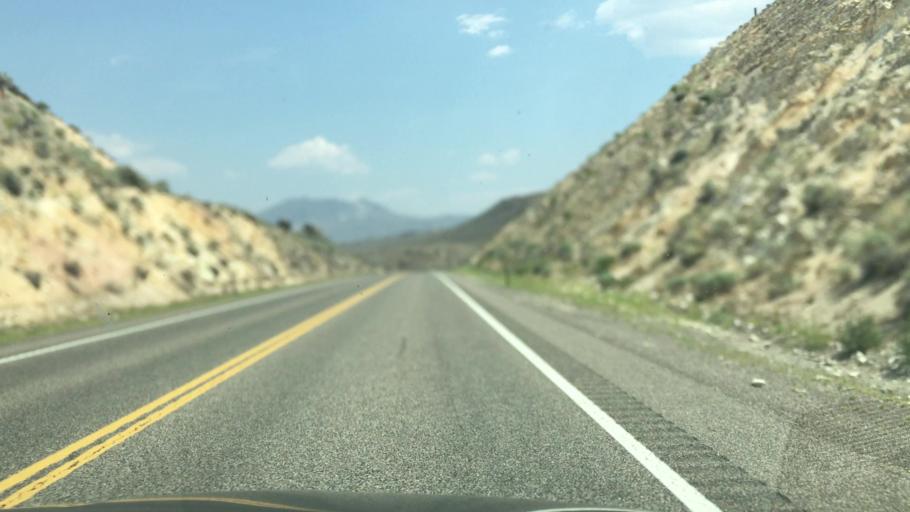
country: US
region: Nevada
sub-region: Elko County
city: Jackpot
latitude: 41.7407
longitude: -114.7789
